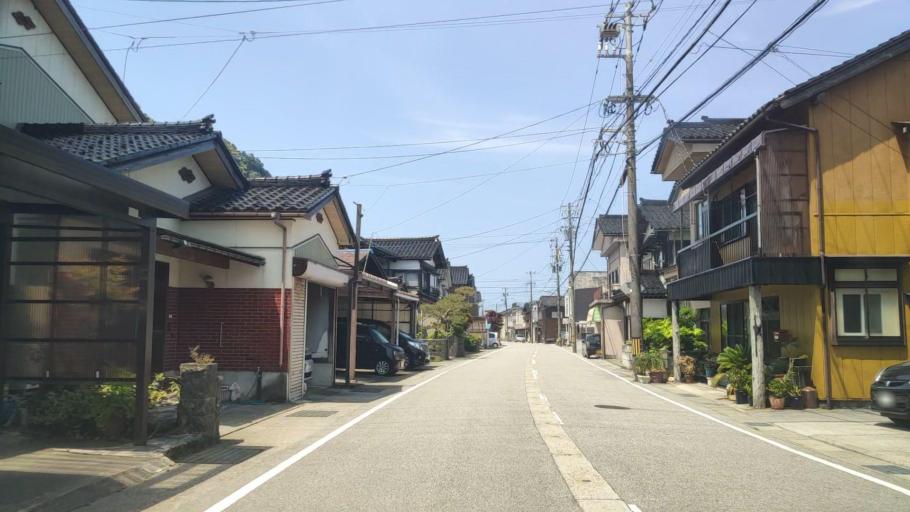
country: JP
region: Toyama
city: Nyuzen
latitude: 36.9729
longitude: 137.5904
